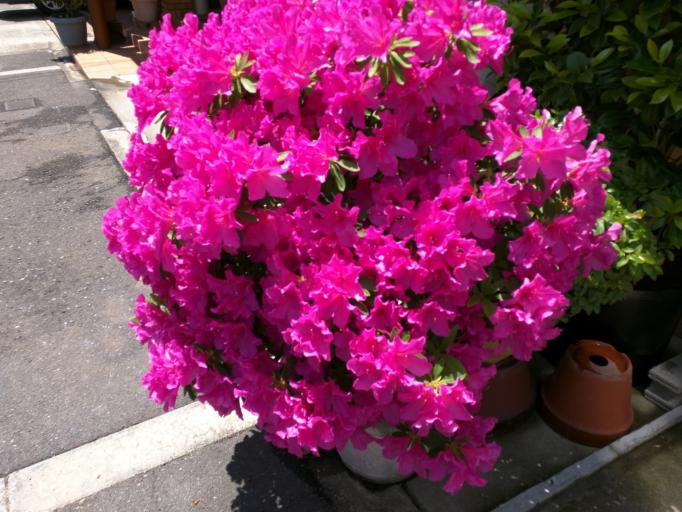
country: JP
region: Osaka
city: Osaka-shi
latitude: 34.6824
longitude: 135.4838
